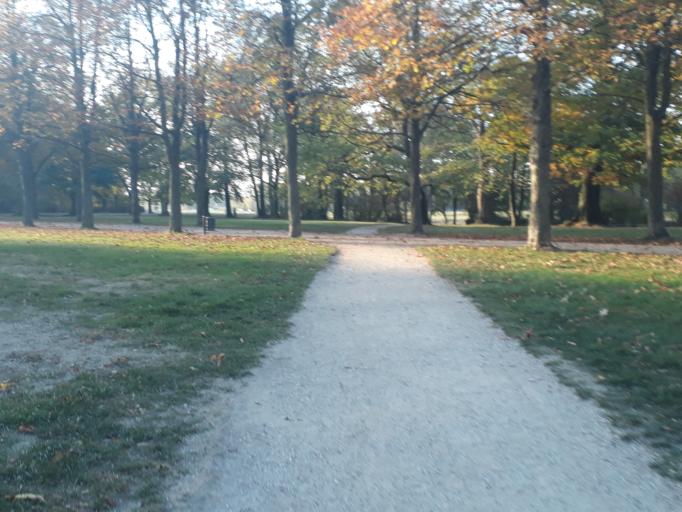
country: DE
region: Saxony
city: Heidenau
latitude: 51.0122
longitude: 13.8645
